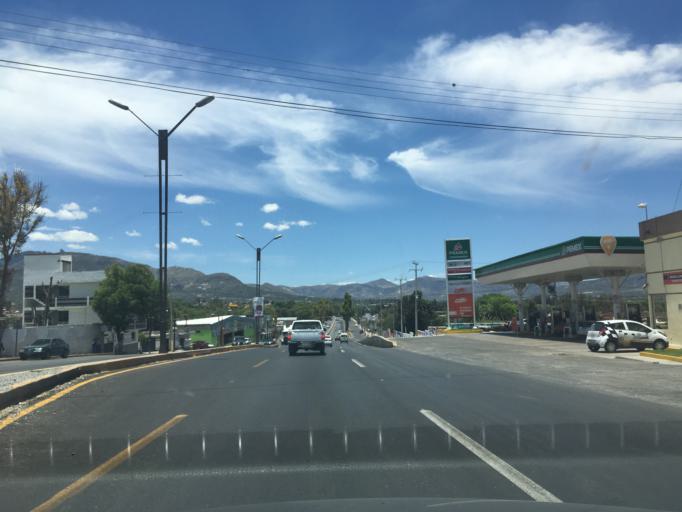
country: MX
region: Hidalgo
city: Actopan
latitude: 20.2617
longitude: -98.9434
